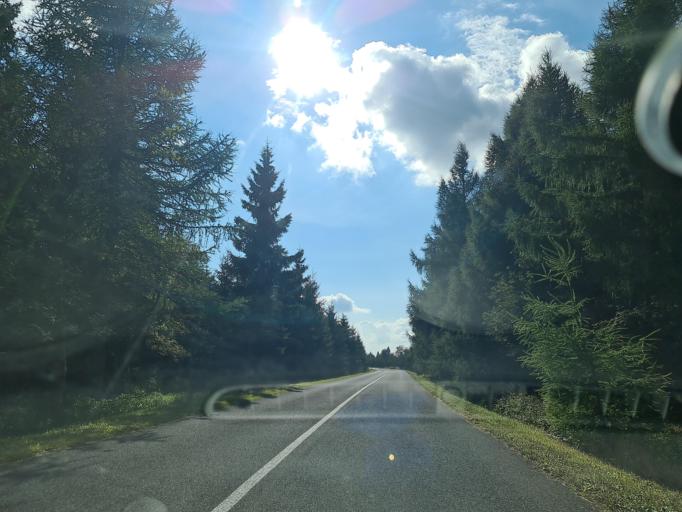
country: CZ
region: Ustecky
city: Mezibori
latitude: 50.6356
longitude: 13.5410
